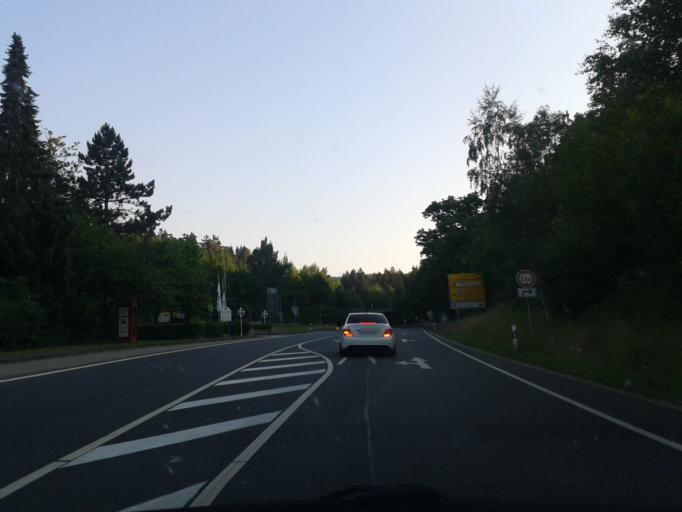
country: DE
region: North Rhine-Westphalia
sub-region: Regierungsbezirk Detmold
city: Horn
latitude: 51.8624
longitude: 8.9315
